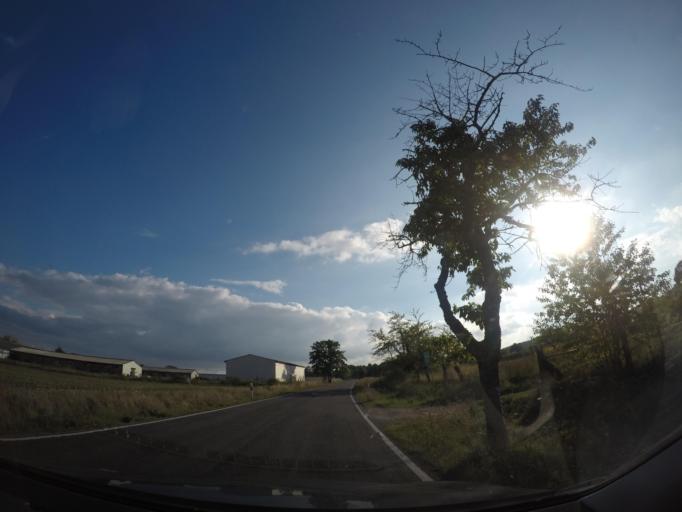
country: DE
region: Saxony-Anhalt
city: Weferlingen
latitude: 52.3226
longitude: 11.0639
